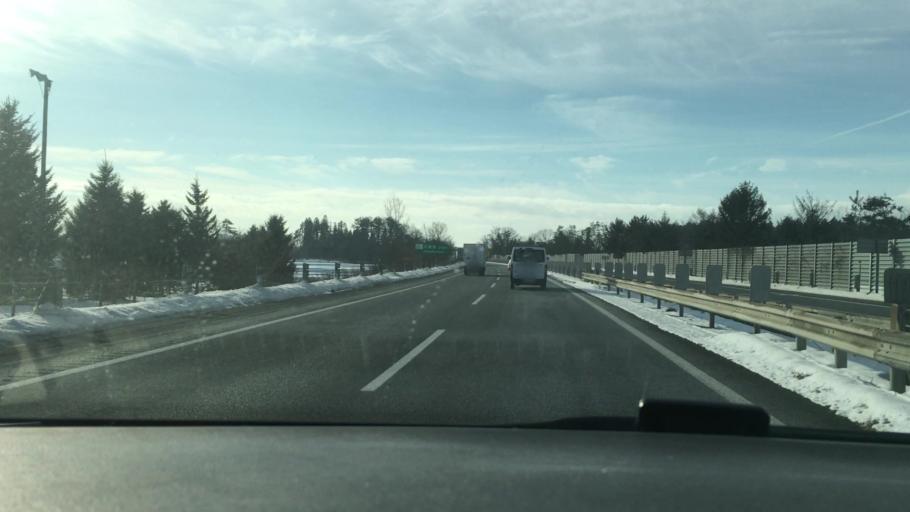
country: JP
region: Iwate
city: Hanamaki
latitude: 39.4064
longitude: 141.0927
